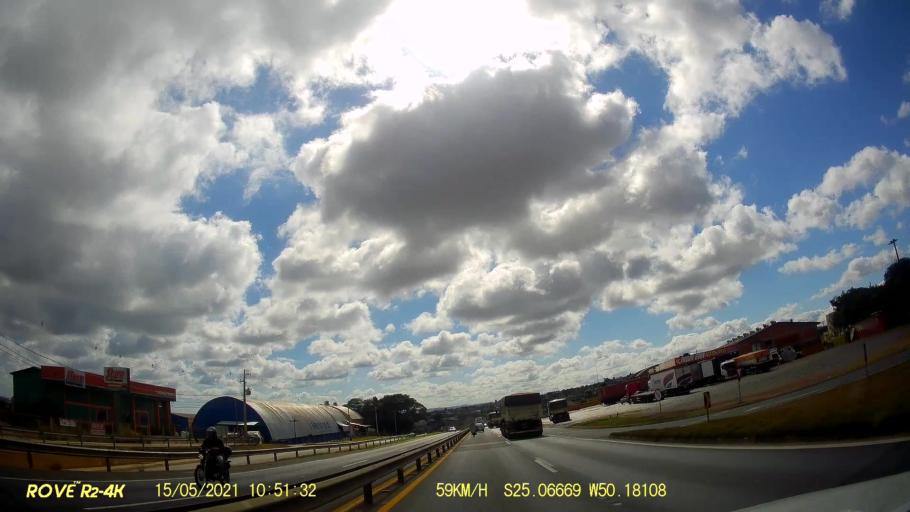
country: BR
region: Parana
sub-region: Ponta Grossa
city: Ponta Grossa
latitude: -25.0668
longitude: -50.1811
